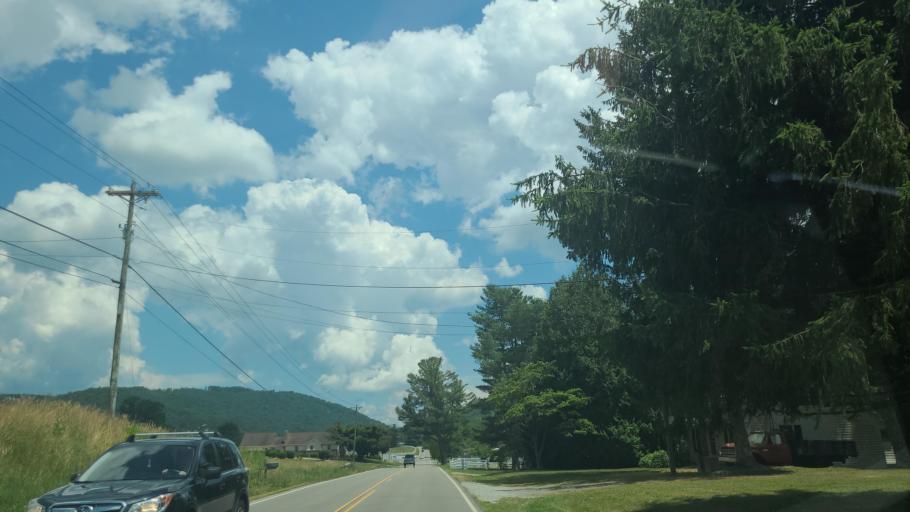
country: US
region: North Carolina
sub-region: Watauga County
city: Boone
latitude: 36.2404
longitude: -81.5265
